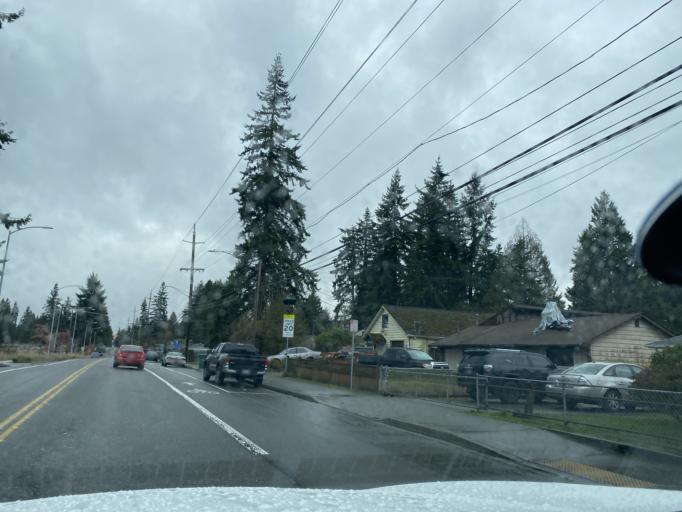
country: US
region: Washington
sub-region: Snohomish County
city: Mountlake Terrace
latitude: 47.8006
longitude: -122.3032
